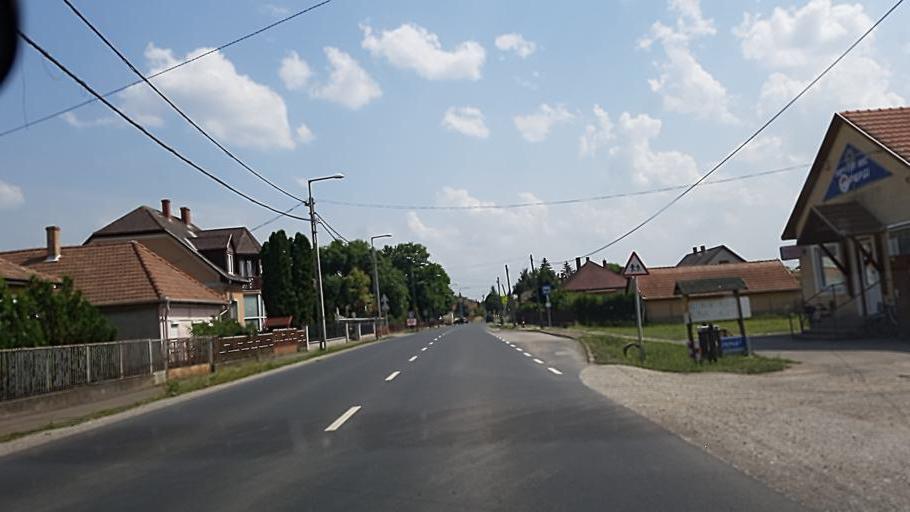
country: HU
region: Heves
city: Besenyotelek
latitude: 47.7066
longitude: 20.4264
